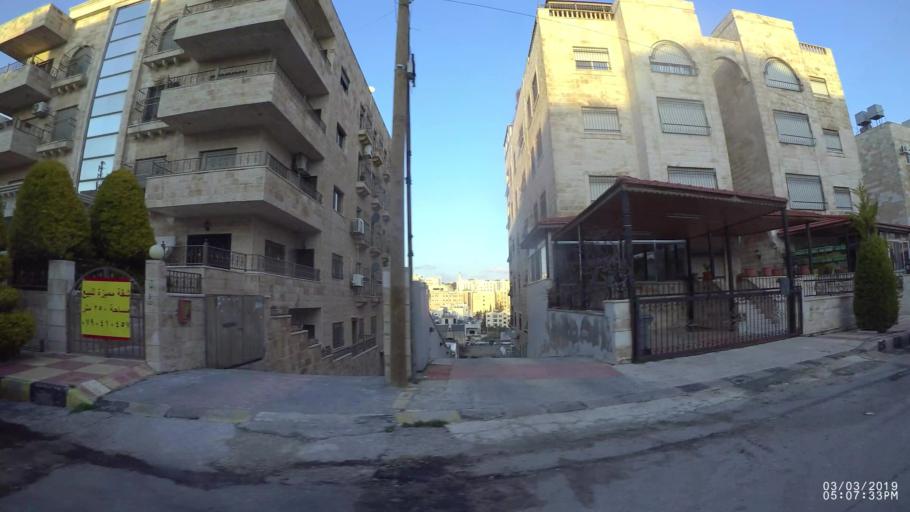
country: JO
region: Amman
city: Al Jubayhah
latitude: 31.9919
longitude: 35.8765
